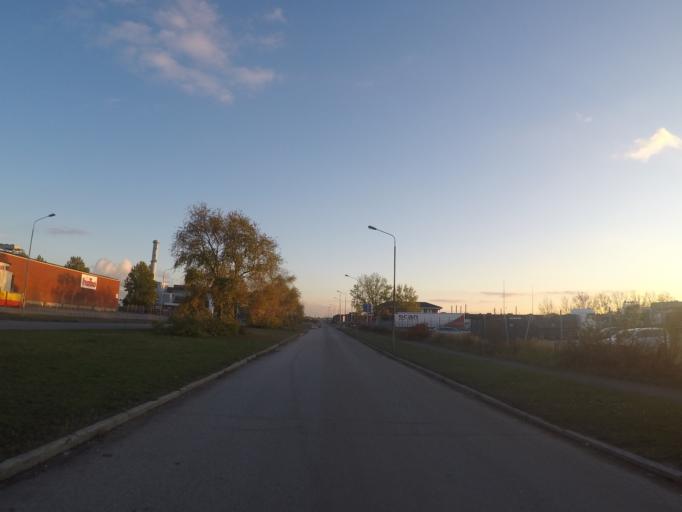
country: SE
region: Skane
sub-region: Burlovs Kommun
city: Arloev
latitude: 55.6308
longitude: 13.0359
